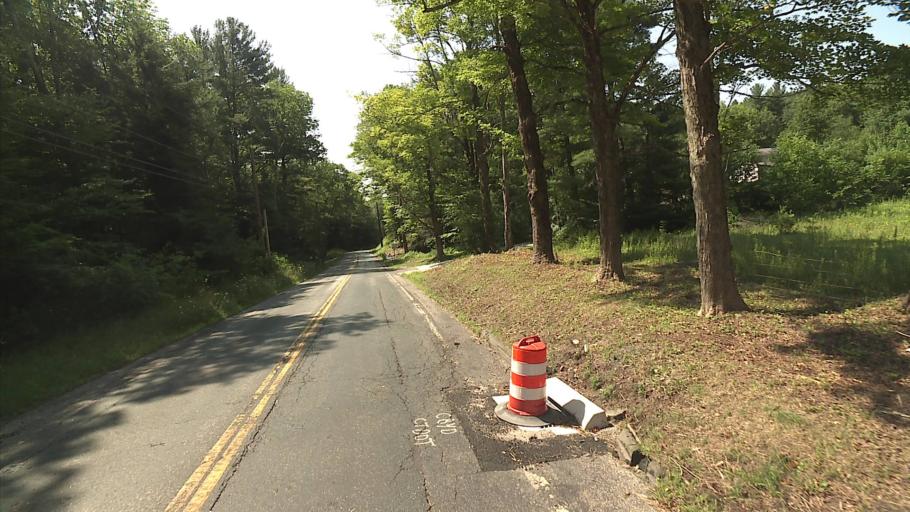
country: US
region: Connecticut
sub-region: Litchfield County
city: Winchester Center
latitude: 41.9378
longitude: -73.2085
